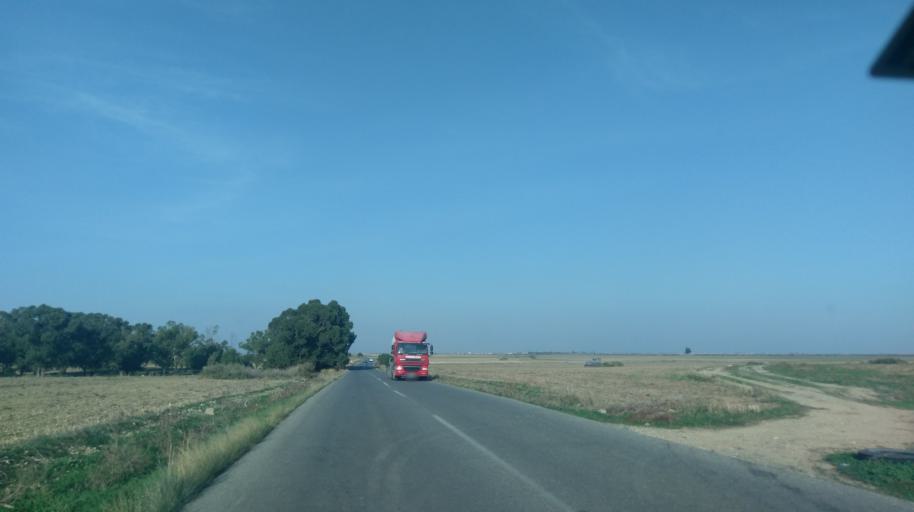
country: CY
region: Ammochostos
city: Achna
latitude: 35.1308
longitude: 33.7376
